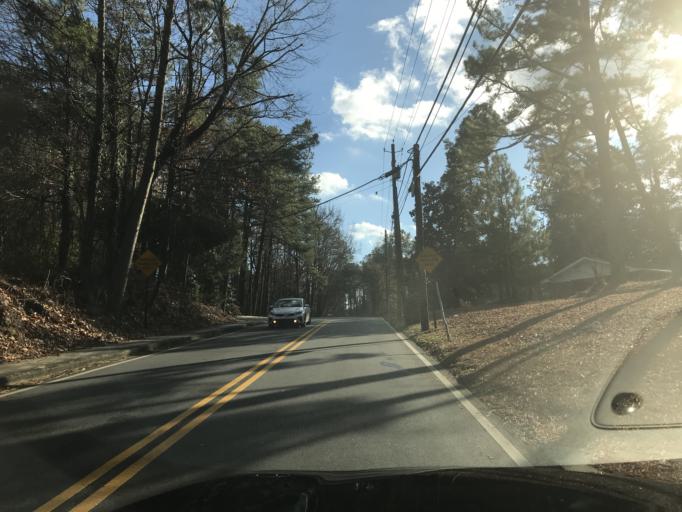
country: US
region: Georgia
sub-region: Fulton County
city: College Park
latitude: 33.6435
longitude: -84.4727
